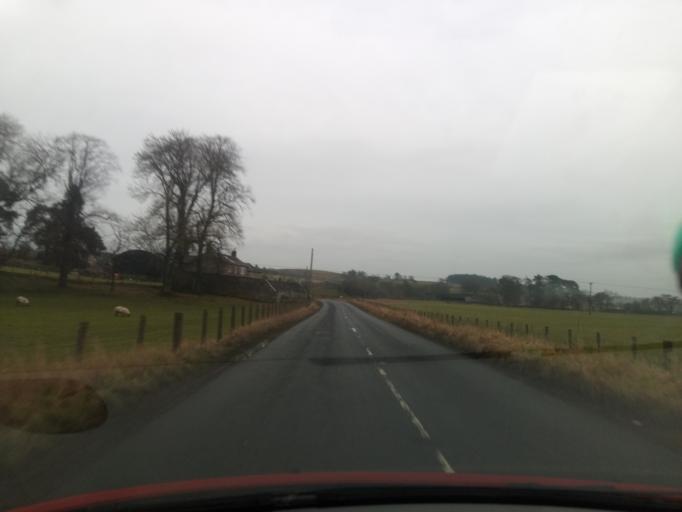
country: GB
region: England
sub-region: Northumberland
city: Rochester
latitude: 55.1647
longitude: -2.3416
